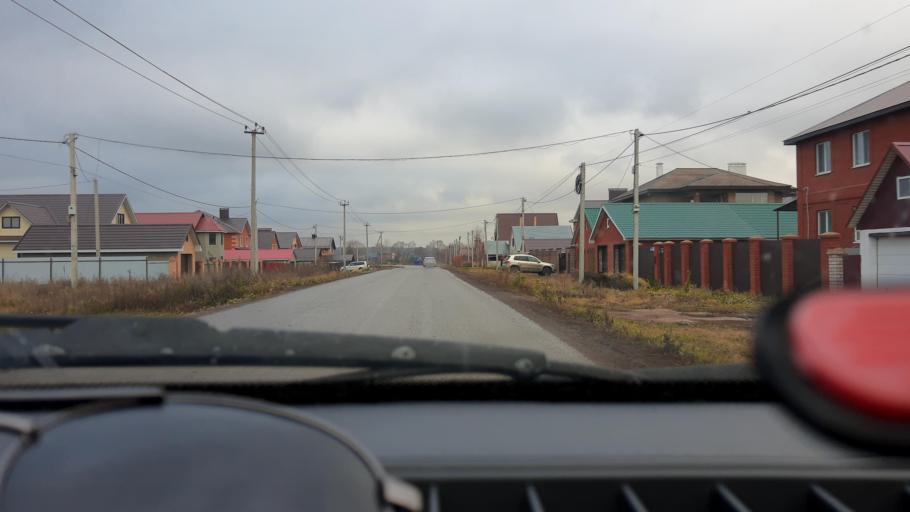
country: RU
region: Bashkortostan
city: Ufa
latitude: 54.6099
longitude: 55.9097
